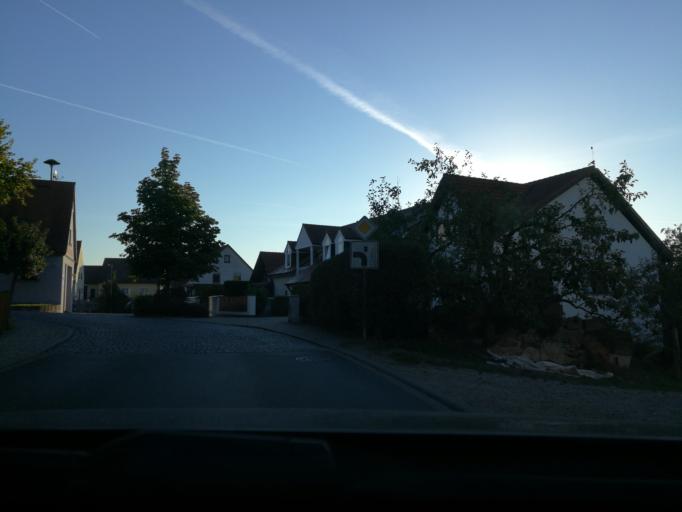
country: DE
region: Bavaria
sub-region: Regierungsbezirk Mittelfranken
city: Herzogenaurach
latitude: 49.5500
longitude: 10.8782
